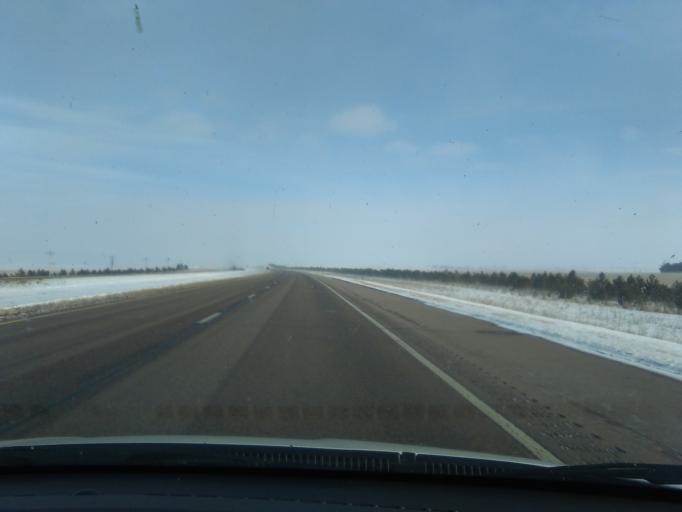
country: US
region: Nebraska
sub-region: Kimball County
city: Kimball
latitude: 41.1931
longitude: -103.7664
